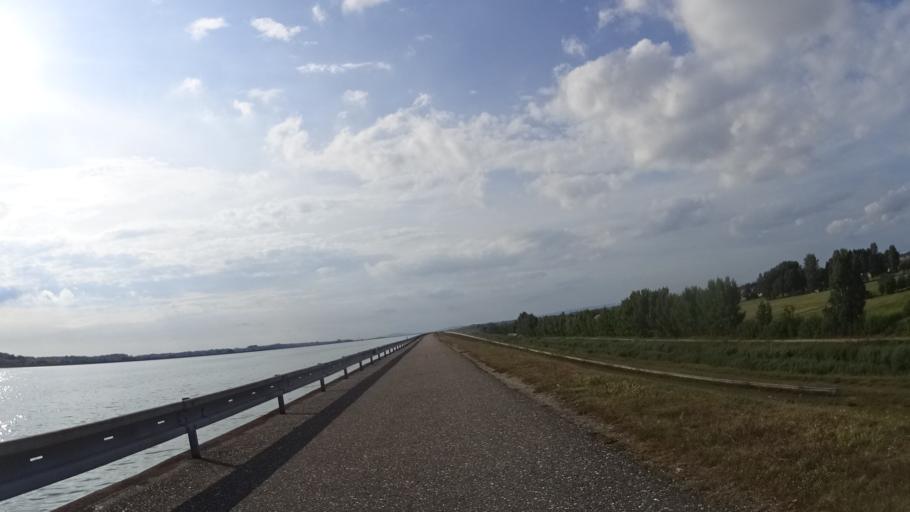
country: HU
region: Gyor-Moson-Sopron
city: Asvanyraro
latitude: 47.9438
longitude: 17.4489
